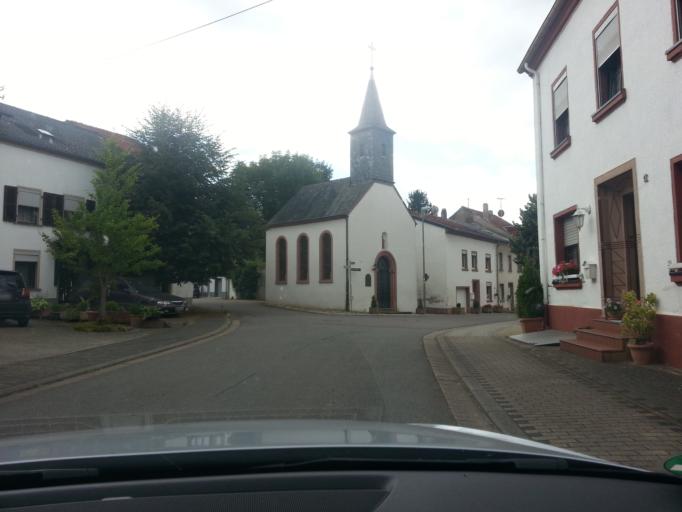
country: LU
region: Grevenmacher
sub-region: Canton de Remich
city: Remich
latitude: 49.5376
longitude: 6.3781
